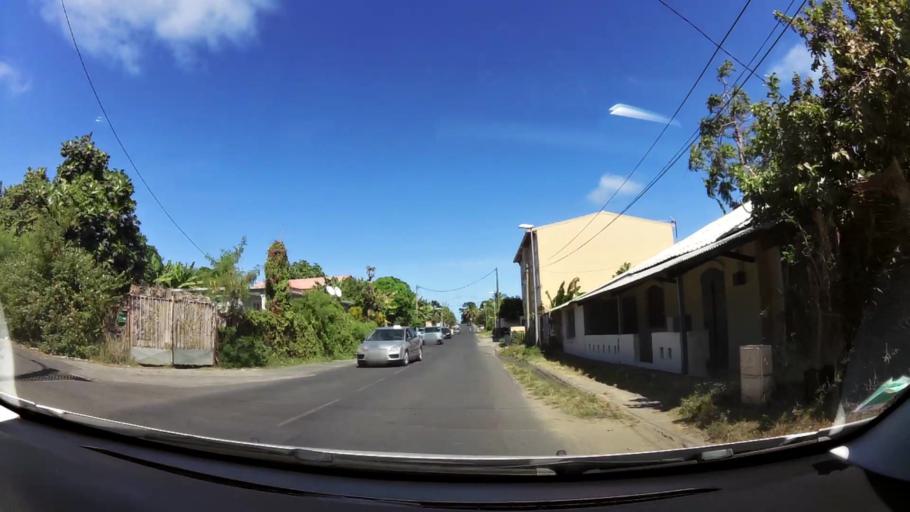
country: YT
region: Pamandzi
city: Pamandzi
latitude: -12.7898
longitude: 45.2799
